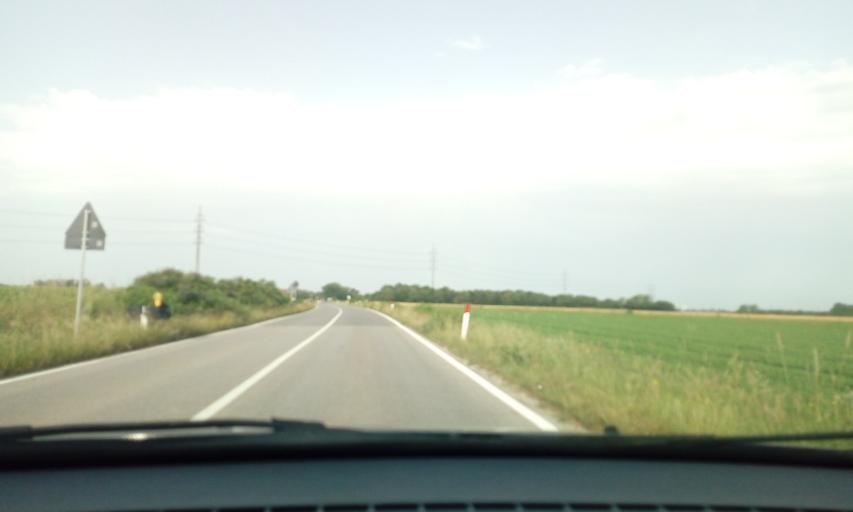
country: IT
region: Friuli Venezia Giulia
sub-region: Provincia di Udine
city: Ialmicco
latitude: 45.9182
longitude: 13.3627
